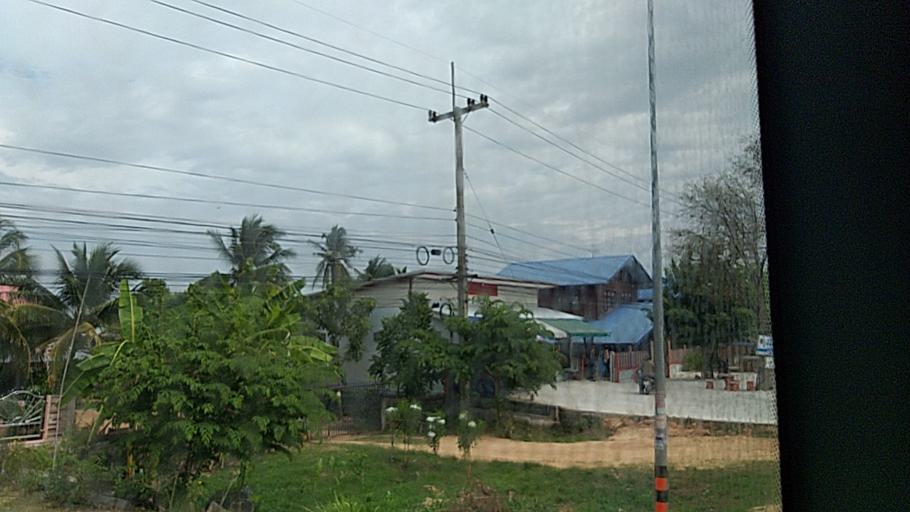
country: TH
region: Maha Sarakham
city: Maha Sarakham
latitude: 16.1520
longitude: 103.3788
